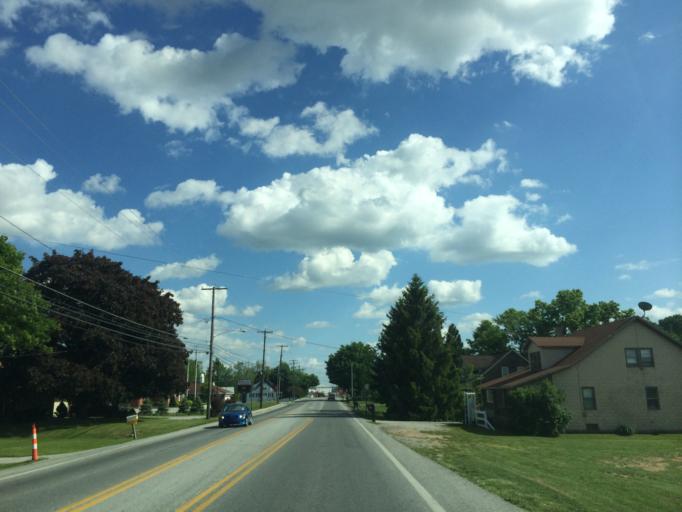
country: US
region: Pennsylvania
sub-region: York County
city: Parkville
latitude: 39.7668
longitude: -76.9607
